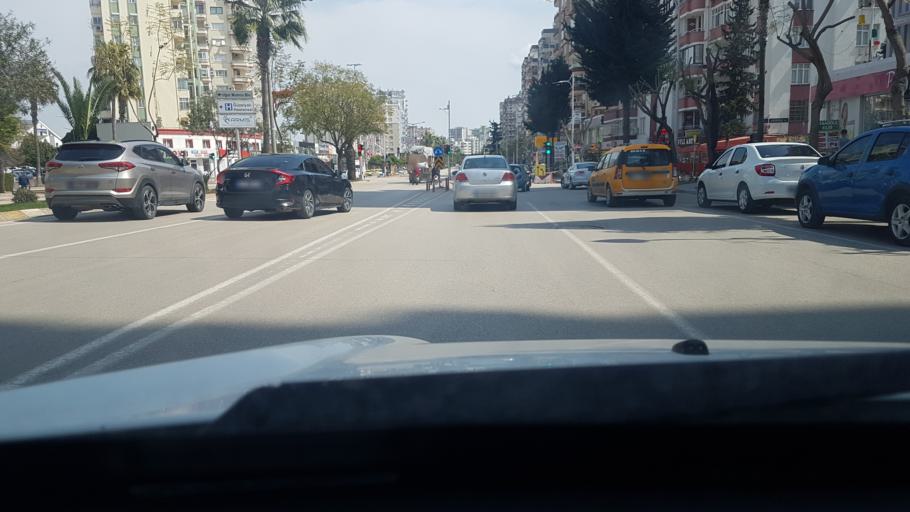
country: TR
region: Adana
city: Adana
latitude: 37.0471
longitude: 35.3012
